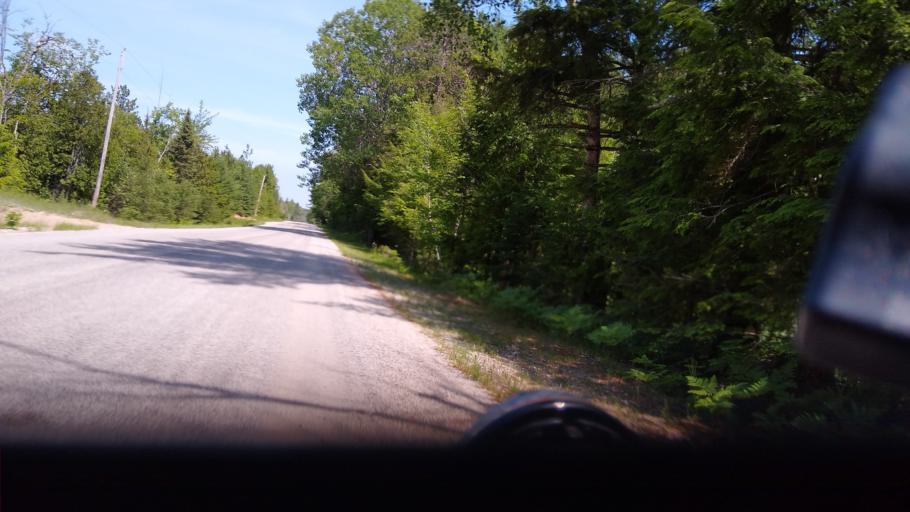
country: US
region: Michigan
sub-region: Delta County
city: Escanaba
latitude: 45.7100
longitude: -87.1528
